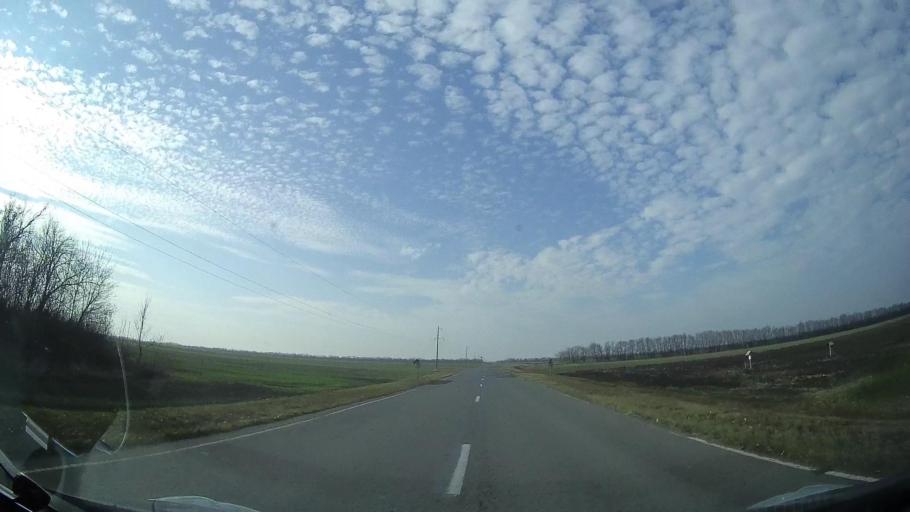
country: RU
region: Rostov
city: Veselyy
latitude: 46.9692
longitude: 40.6832
